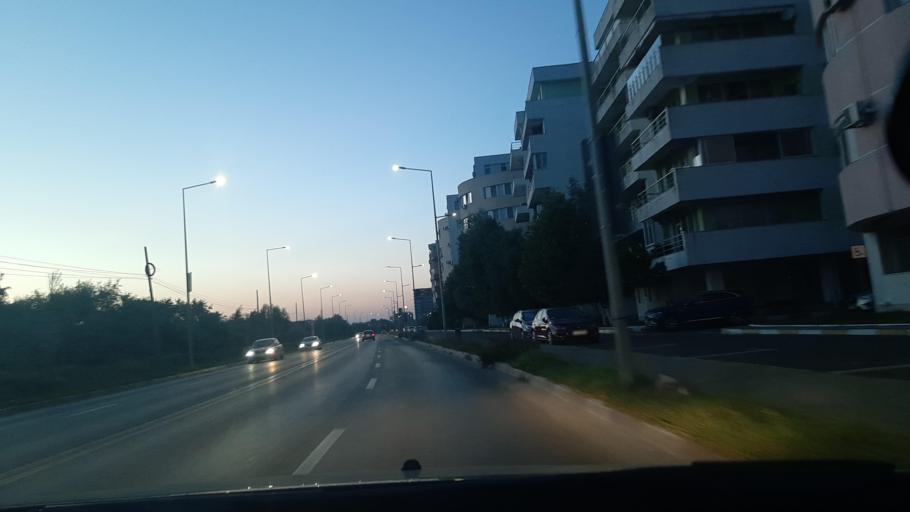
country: RO
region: Constanta
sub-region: Municipiul Constanta
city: Palazu Mare
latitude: 44.2664
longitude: 28.6182
